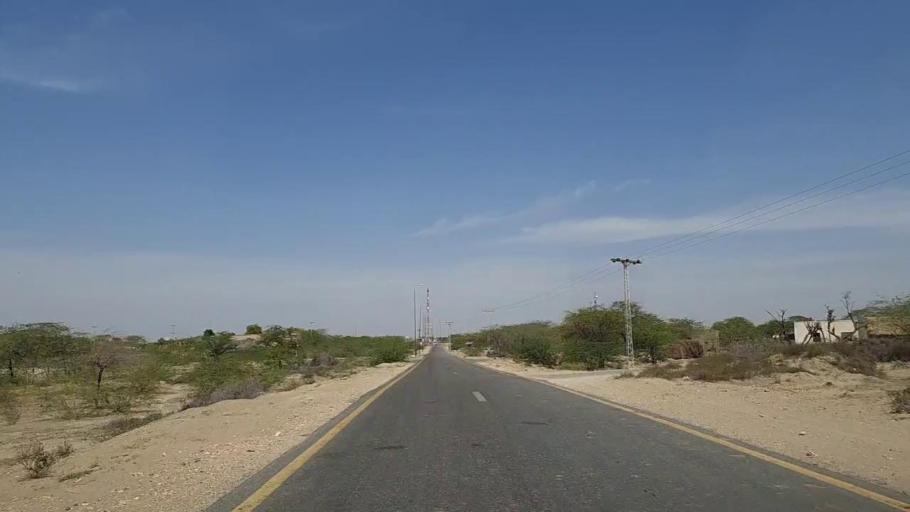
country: PK
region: Sindh
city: Mithi
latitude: 24.9710
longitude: 69.9146
